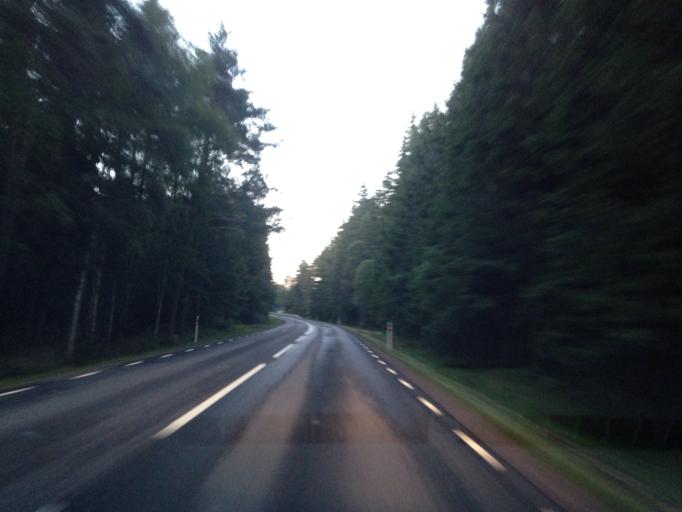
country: SE
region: Vaestra Goetaland
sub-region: Tranemo Kommun
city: Langhem
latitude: 57.6033
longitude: 13.1347
